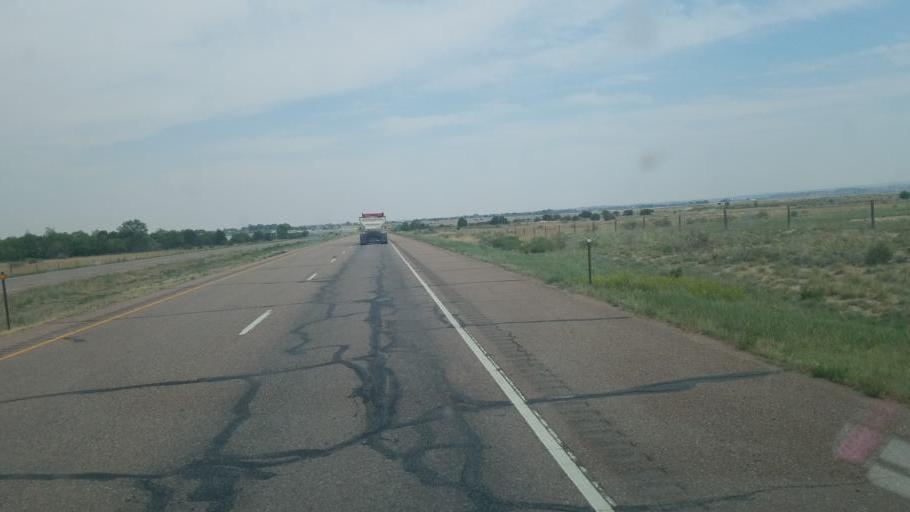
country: US
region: Colorado
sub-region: Fremont County
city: Penrose
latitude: 38.4135
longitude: -105.0225
